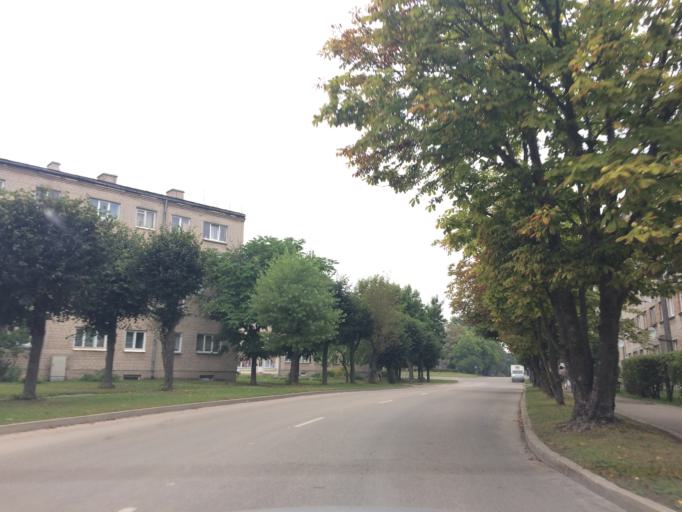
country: LV
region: Rezekne
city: Rezekne
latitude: 56.5015
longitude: 27.3236
